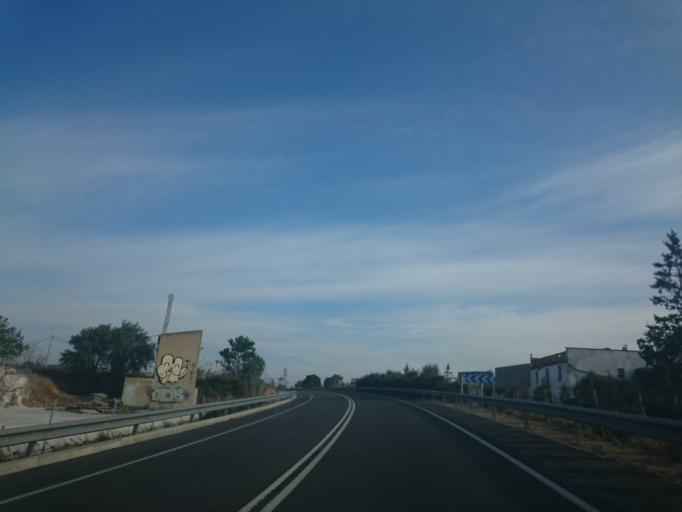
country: ES
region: Catalonia
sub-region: Provincia de Barcelona
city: La Granada
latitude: 41.3786
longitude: 1.7128
